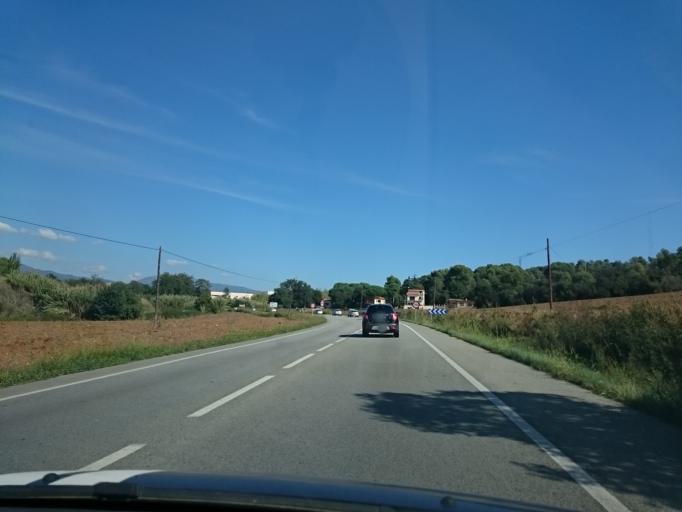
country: ES
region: Catalonia
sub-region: Provincia de Barcelona
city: Les Franqueses del Valles
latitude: 41.6216
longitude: 2.3202
